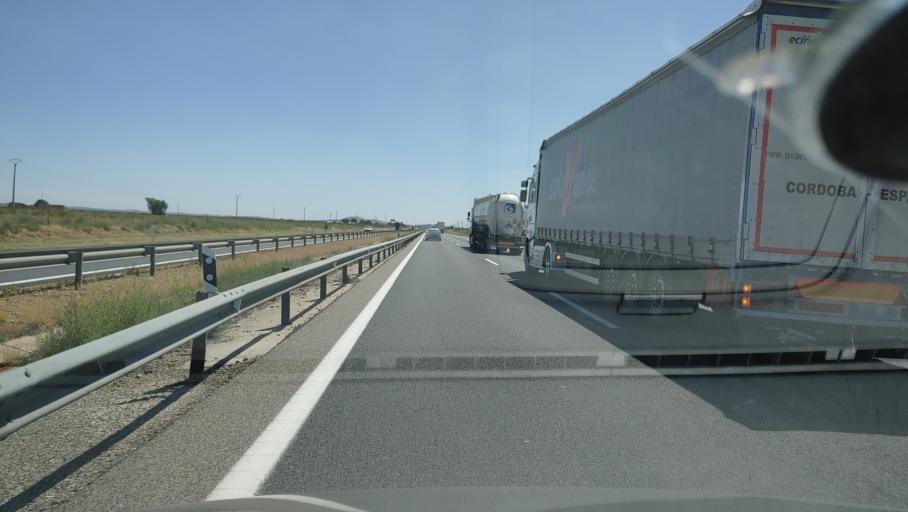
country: ES
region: Castille-La Mancha
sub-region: Provincia de Ciudad Real
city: Valdepenas
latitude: 38.8672
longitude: -3.3933
